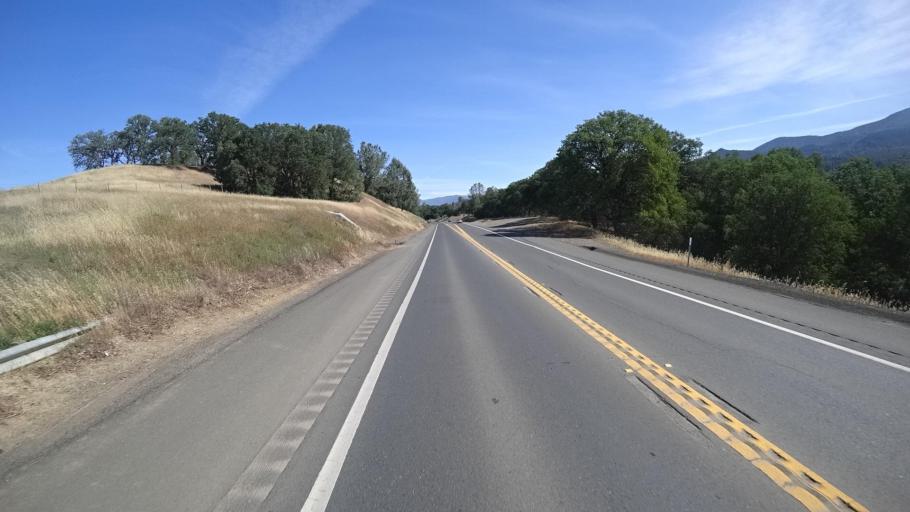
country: US
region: California
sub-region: Lake County
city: Kelseyville
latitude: 38.9650
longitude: -122.8293
